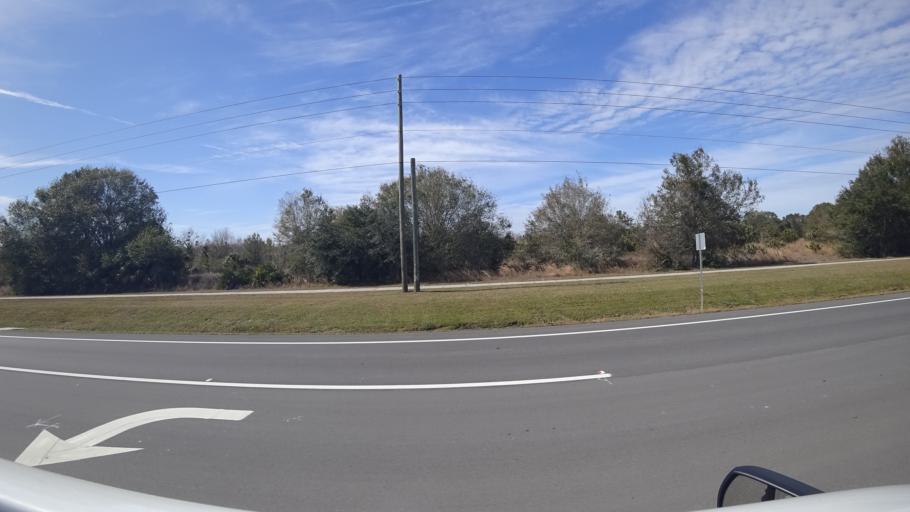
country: US
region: Florida
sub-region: Manatee County
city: Ellenton
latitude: 27.5462
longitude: -82.4254
